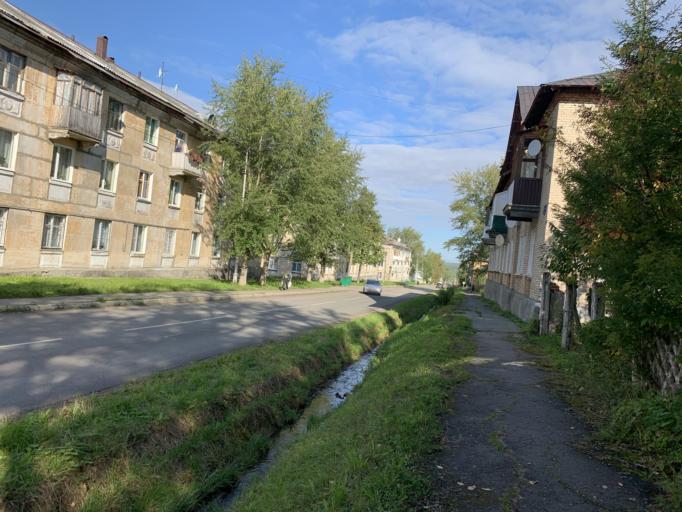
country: RU
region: Perm
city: Gubakha
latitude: 58.8385
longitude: 57.5566
